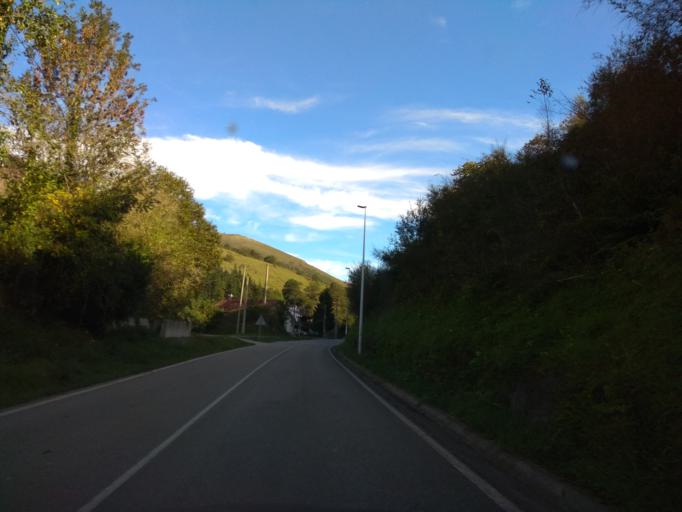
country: ES
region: Cantabria
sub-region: Provincia de Cantabria
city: Ruente
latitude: 43.2231
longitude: -4.3881
